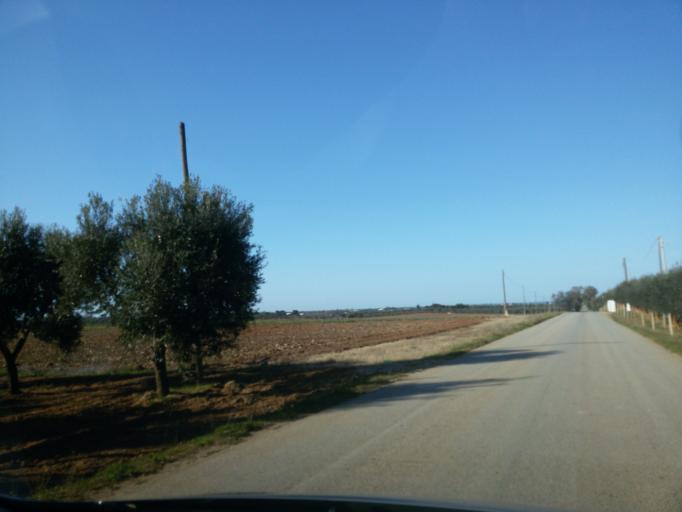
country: IT
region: Apulia
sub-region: Provincia di Brindisi
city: Mesagne
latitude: 40.6670
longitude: 17.8197
